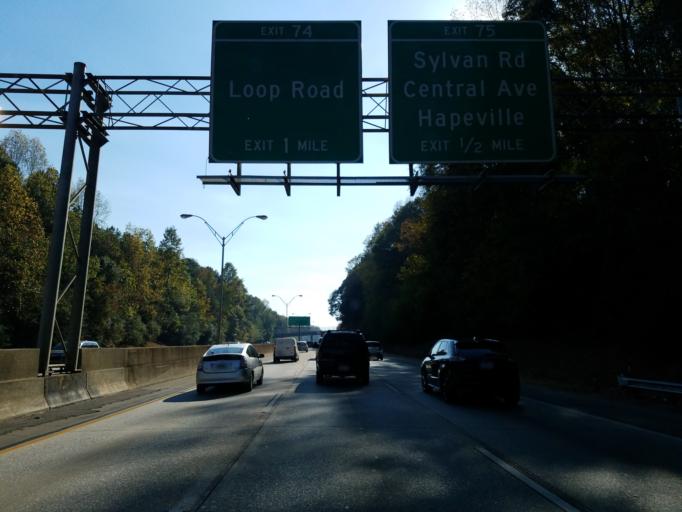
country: US
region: Georgia
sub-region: Fulton County
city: Hapeville
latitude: 33.6750
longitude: -84.4137
